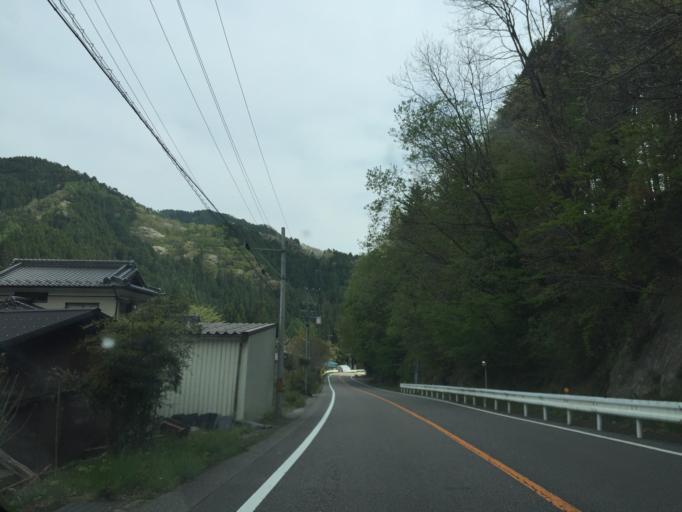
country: JP
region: Gifu
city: Nakatsugawa
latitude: 35.2180
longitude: 137.6846
